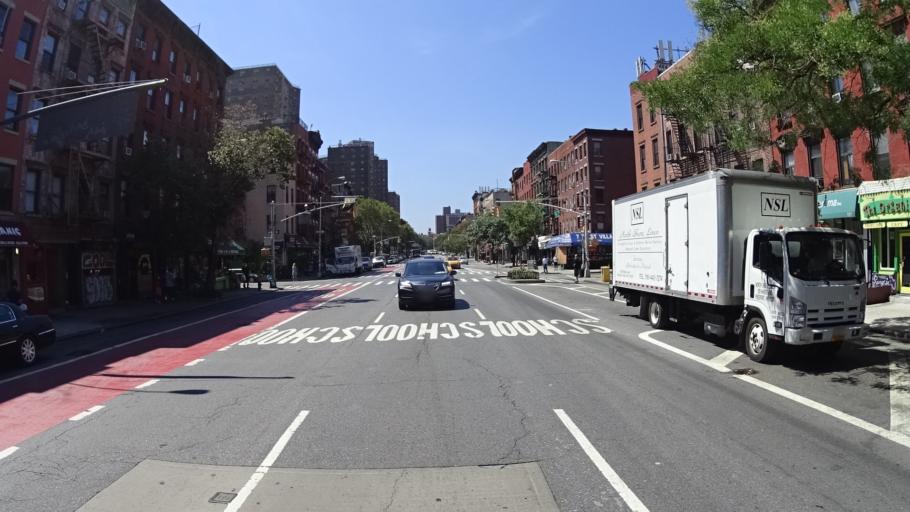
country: US
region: New York
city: New York City
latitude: 40.7274
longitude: -73.9855
